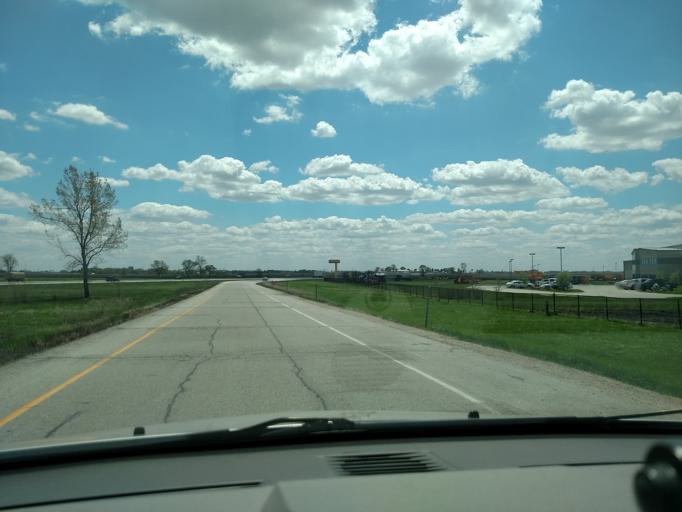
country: US
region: Iowa
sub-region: Polk County
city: Ankeny
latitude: 41.7905
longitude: -93.5721
